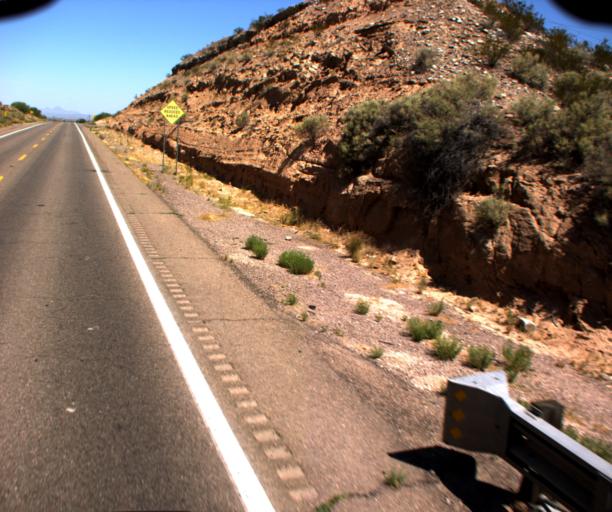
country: US
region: Arizona
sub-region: Graham County
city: Bylas
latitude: 33.1039
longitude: -110.0834
